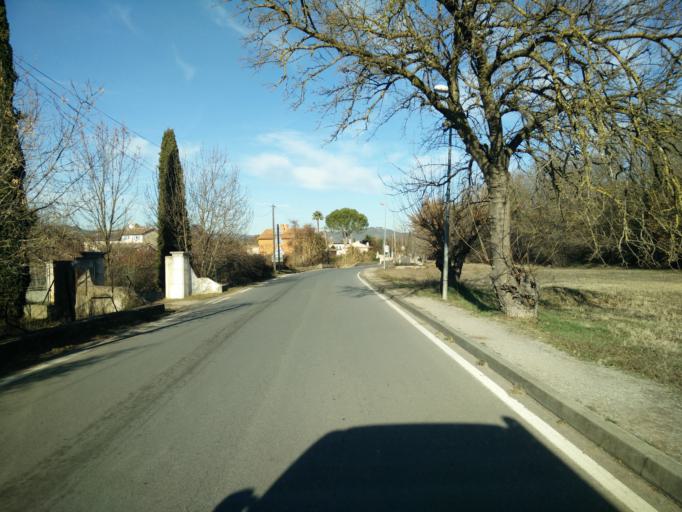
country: FR
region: Provence-Alpes-Cote d'Azur
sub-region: Departement du Var
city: Vidauban
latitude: 43.4173
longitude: 6.4276
